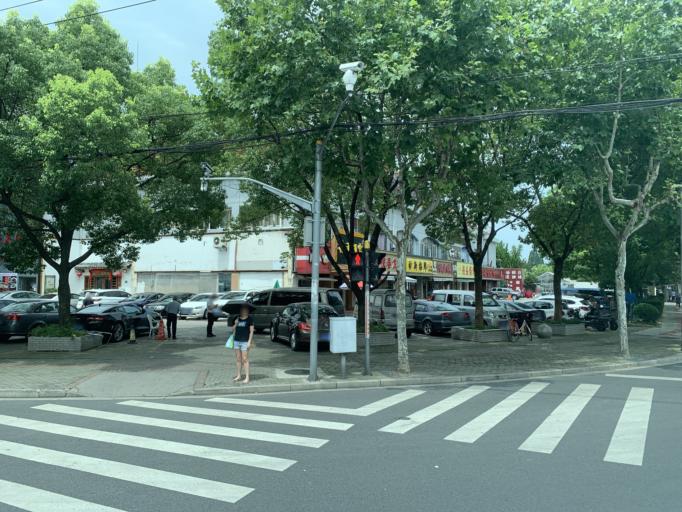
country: CN
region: Shanghai Shi
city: Pudong
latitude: 31.2463
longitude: 121.5622
